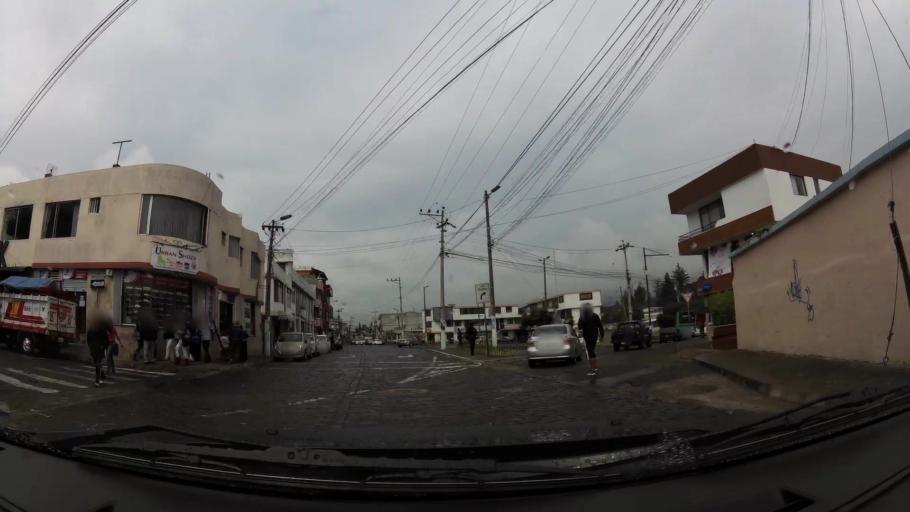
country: EC
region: Pichincha
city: Sangolqui
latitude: -0.2927
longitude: -78.4786
